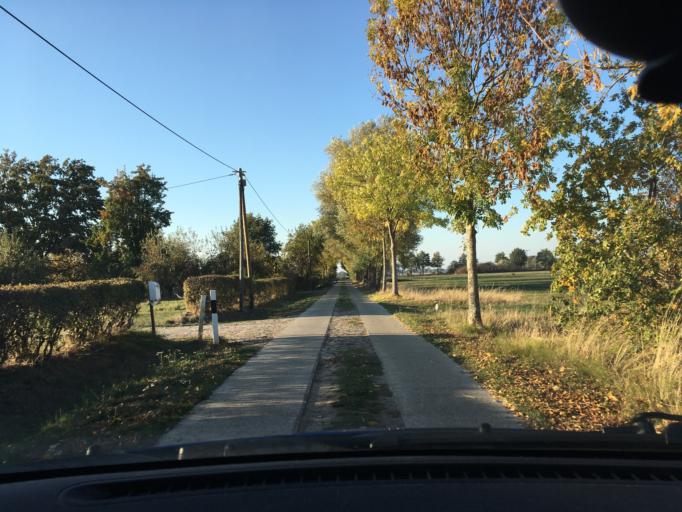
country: DE
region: Lower Saxony
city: Bleckede
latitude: 53.2872
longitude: 10.8061
